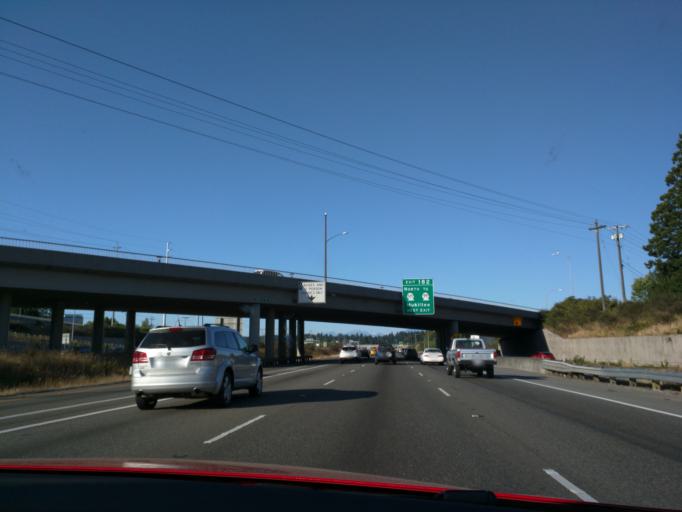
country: US
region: Washington
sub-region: Snohomish County
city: Alderwood Manor
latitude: 47.8204
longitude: -122.2796
